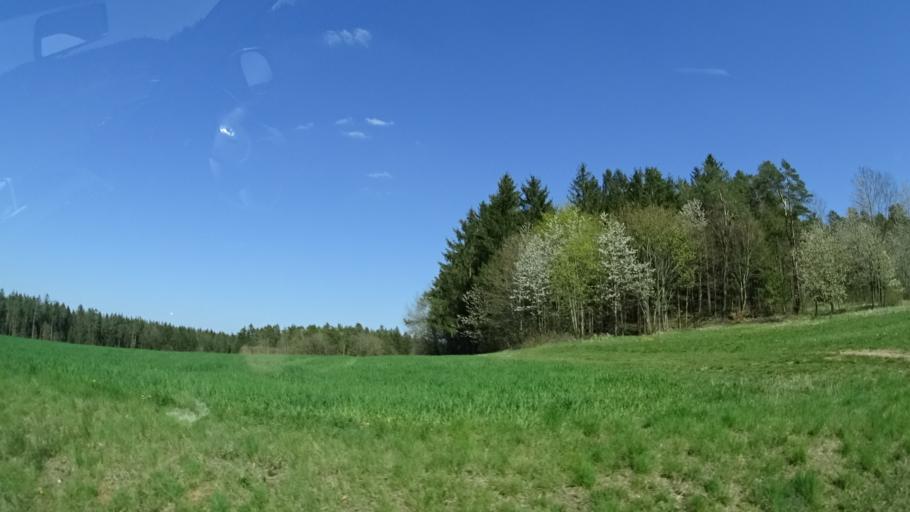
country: DE
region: Bavaria
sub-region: Upper Palatinate
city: Illschwang
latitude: 49.5006
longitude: 11.6536
